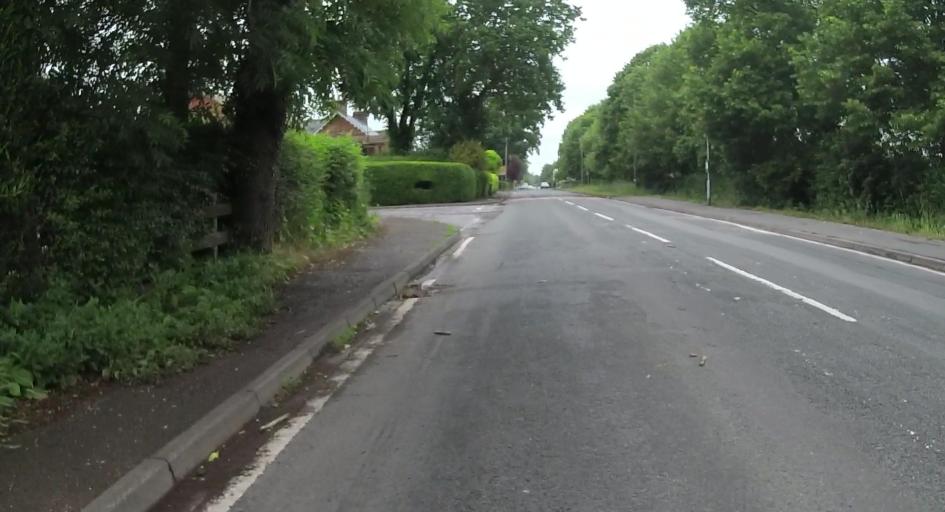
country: GB
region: England
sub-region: Wokingham
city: Swallowfield
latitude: 51.3614
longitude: -0.9632
